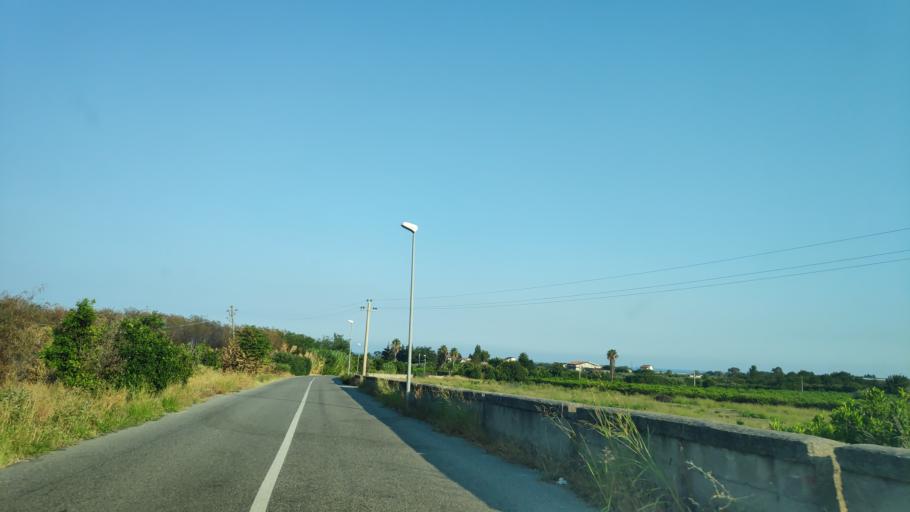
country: IT
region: Calabria
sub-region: Provincia di Reggio Calabria
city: Caulonia Marina
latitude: 38.3612
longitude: 16.4645
